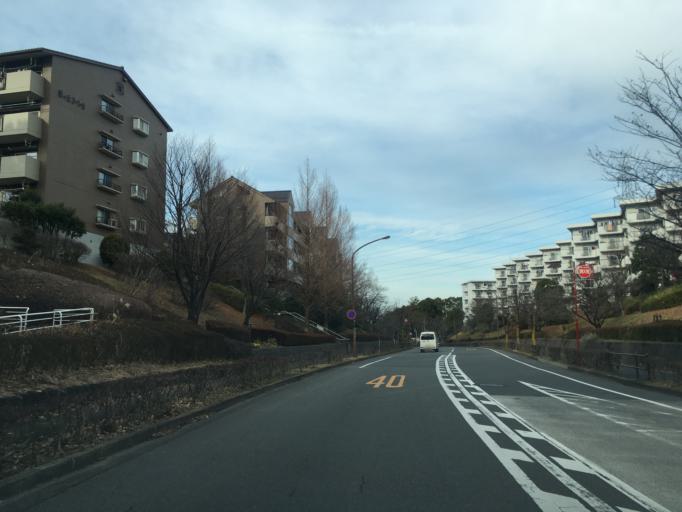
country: JP
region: Tokyo
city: Hino
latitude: 35.6181
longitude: 139.4372
